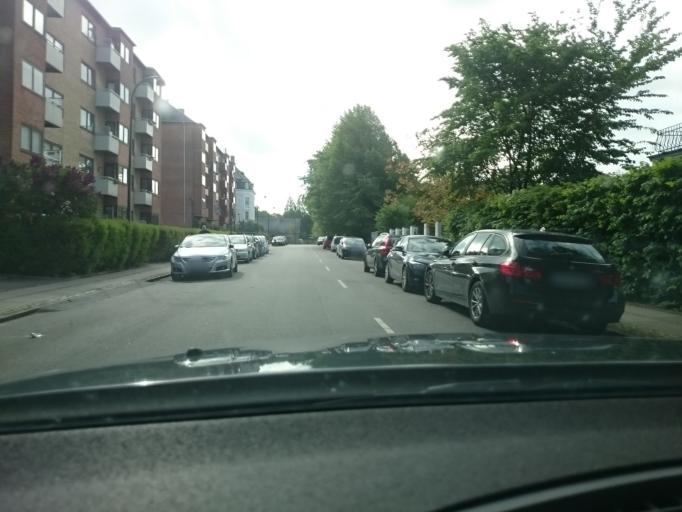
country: DK
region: Capital Region
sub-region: Gentofte Kommune
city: Charlottenlund
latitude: 55.7522
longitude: 12.5693
